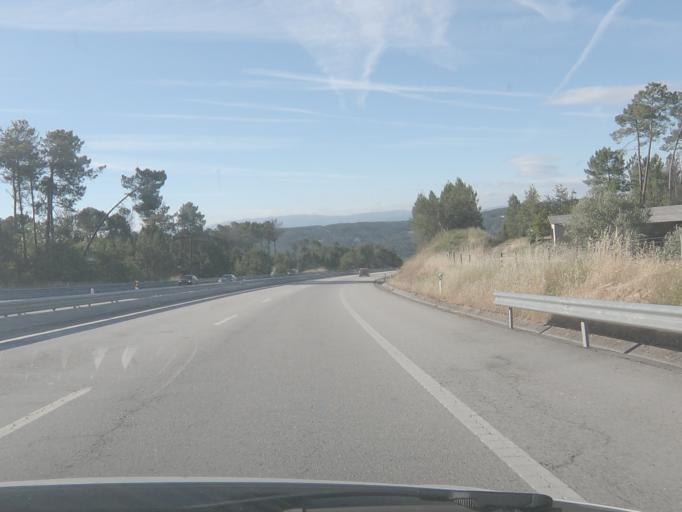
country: PT
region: Viseu
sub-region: Viseu
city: Campo
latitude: 40.7376
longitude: -7.9244
